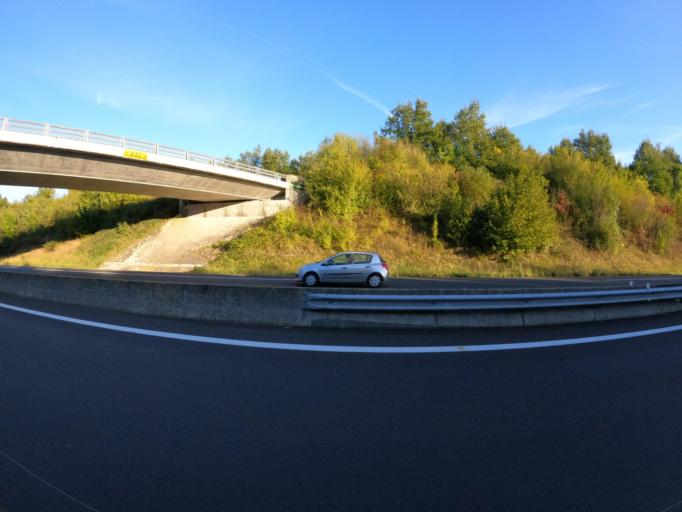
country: FR
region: Pays de la Loire
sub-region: Departement de la Vendee
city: Beaurepaire
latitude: 46.8855
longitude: -1.1030
